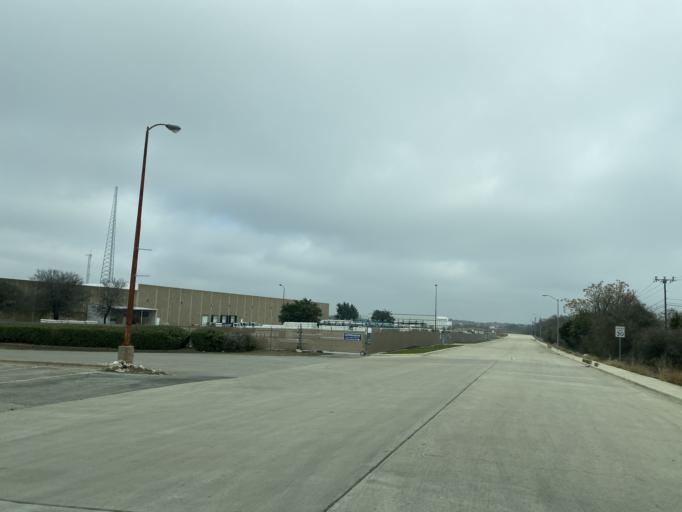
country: US
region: Texas
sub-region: Williamson County
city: Round Rock
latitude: 30.5374
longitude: -97.6882
